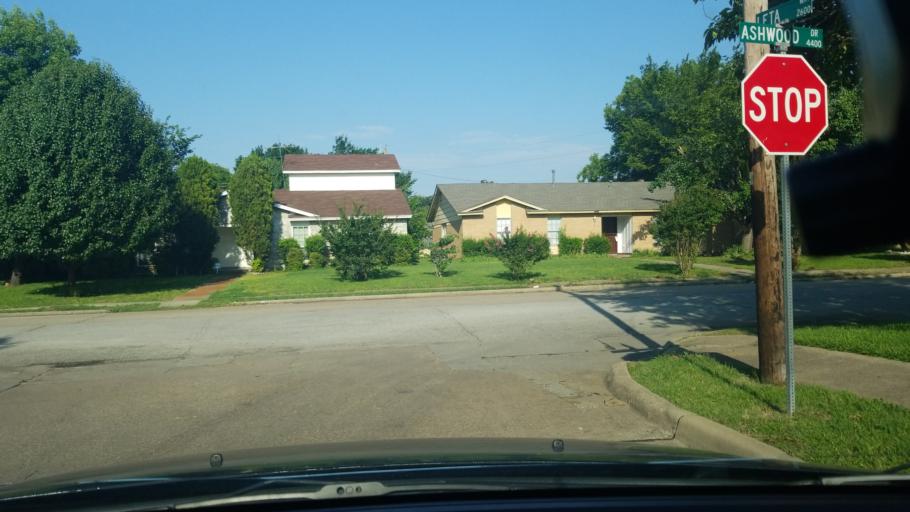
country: US
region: Texas
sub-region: Dallas County
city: Mesquite
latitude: 32.8265
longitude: -96.6378
